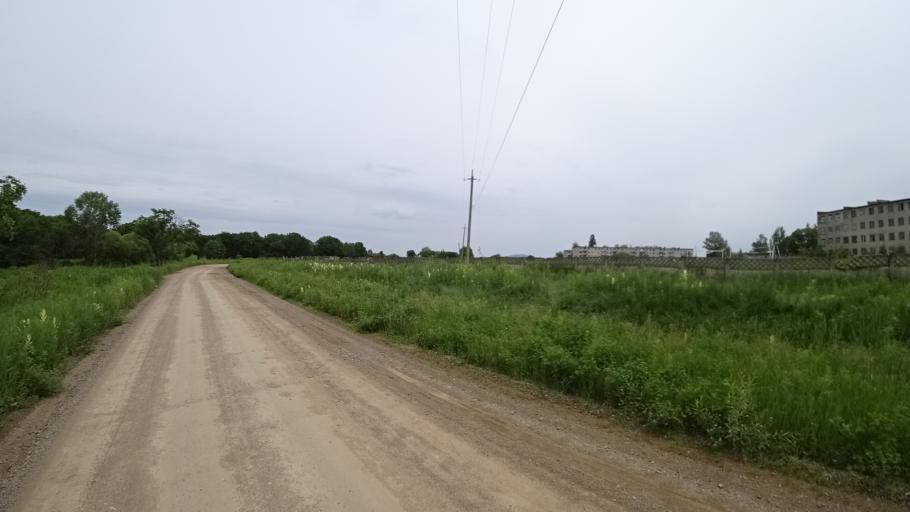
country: RU
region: Primorskiy
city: Arsen'yev
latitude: 44.2008
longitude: 133.3108
